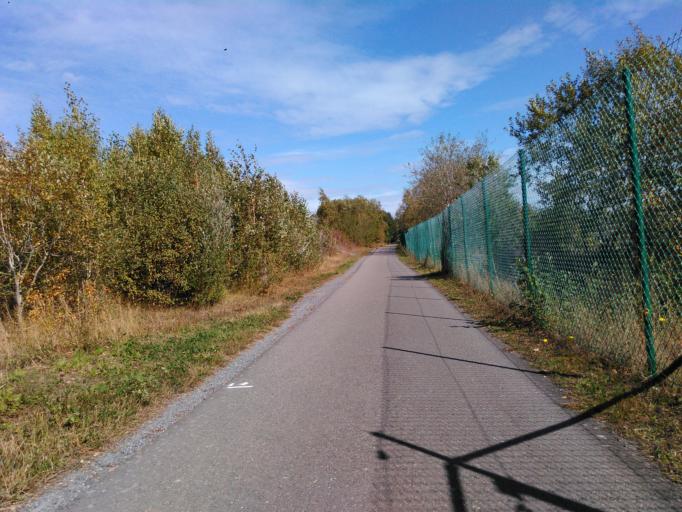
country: BE
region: Wallonia
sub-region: Province du Luxembourg
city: Bastogne
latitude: 50.0135
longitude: 5.7370
